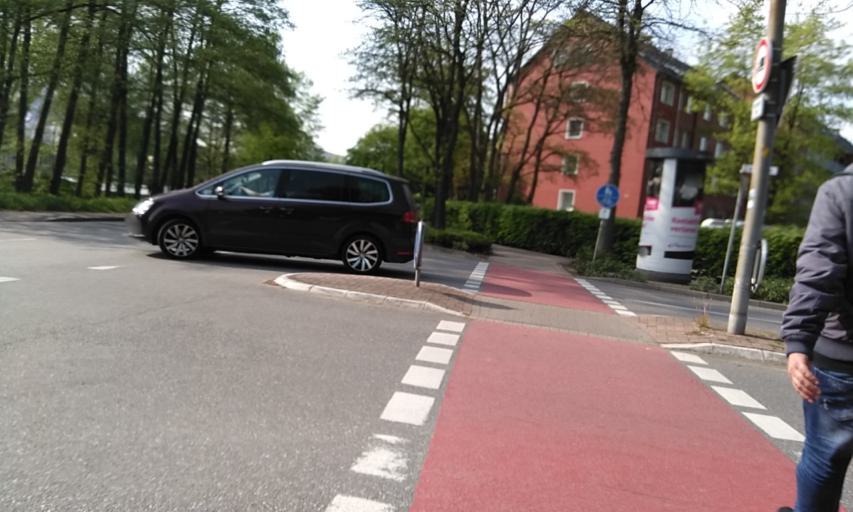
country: DE
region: Lower Saxony
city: Buxtehude
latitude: 53.4634
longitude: 9.6948
